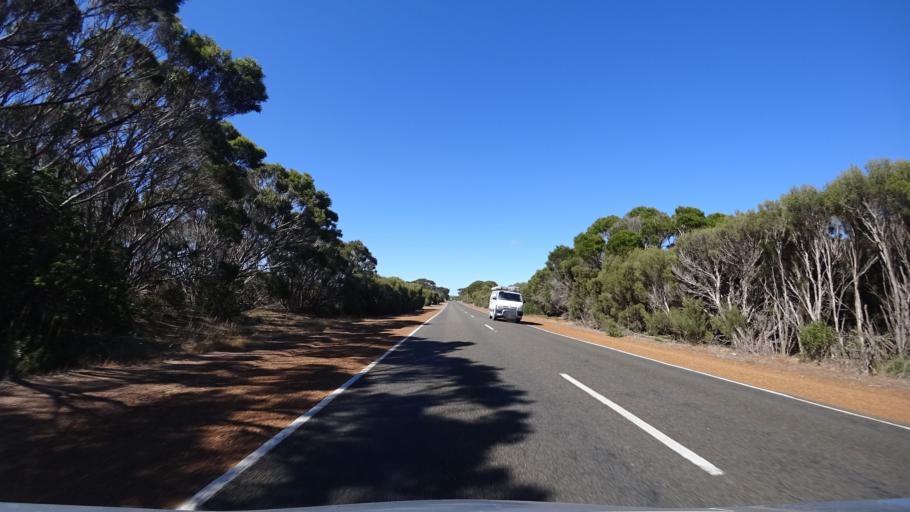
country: AU
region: South Australia
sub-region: Kangaroo Island
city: Kingscote
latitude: -35.7068
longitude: 137.5662
